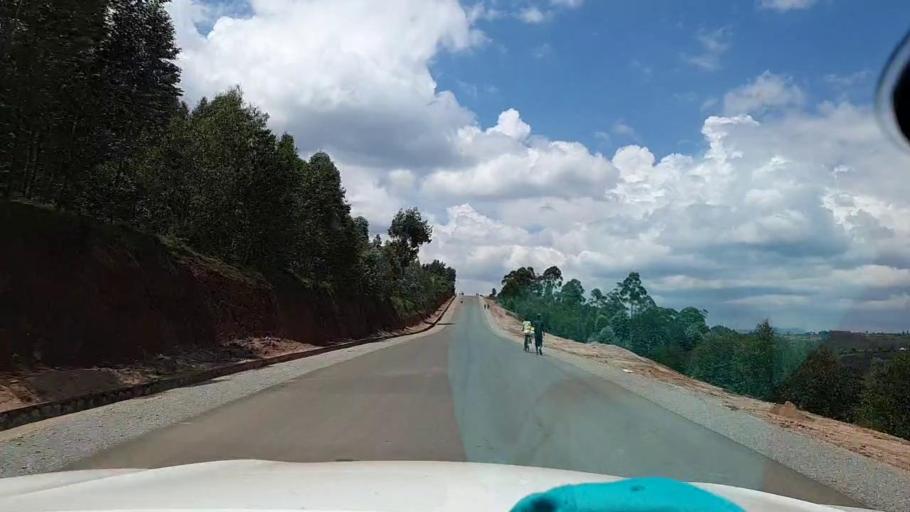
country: RW
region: Southern Province
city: Nzega
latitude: -2.6426
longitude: 29.5753
